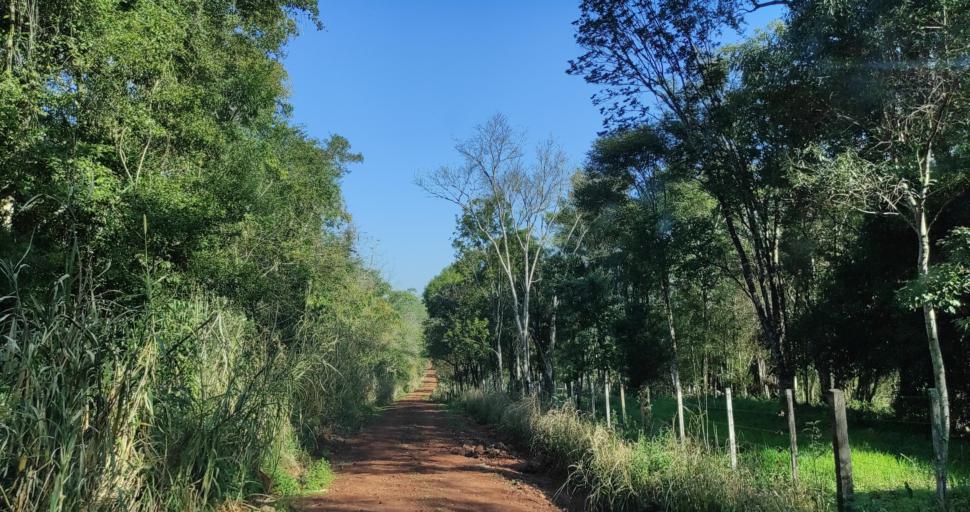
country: AR
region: Misiones
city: Capiovi
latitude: -26.8959
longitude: -55.1072
